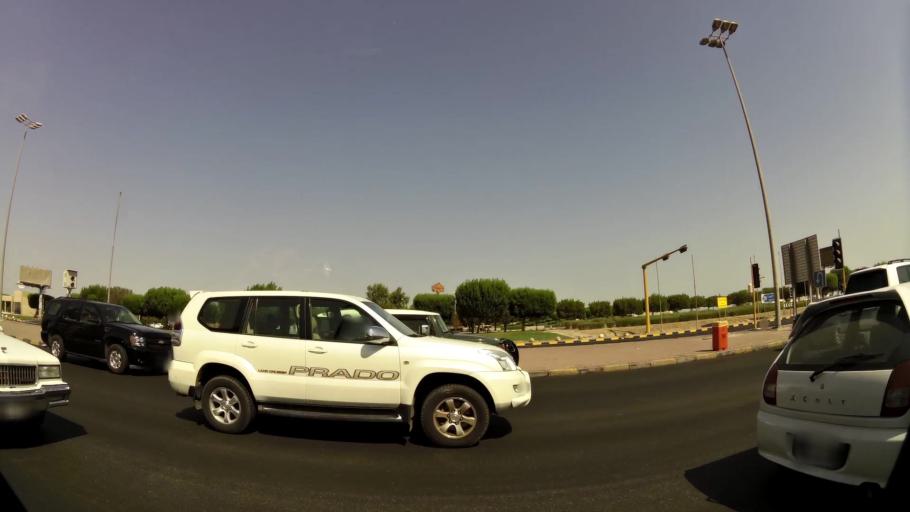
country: KW
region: Al Asimah
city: Ad Dasmah
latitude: 29.3689
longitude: 48.0124
